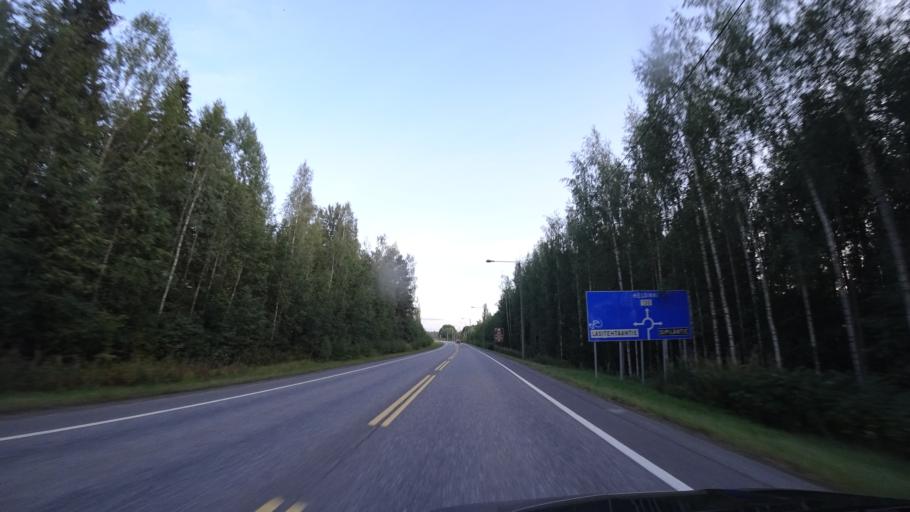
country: FI
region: Haeme
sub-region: Riihimaeki
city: Riihimaeki
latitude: 60.7404
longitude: 24.7313
